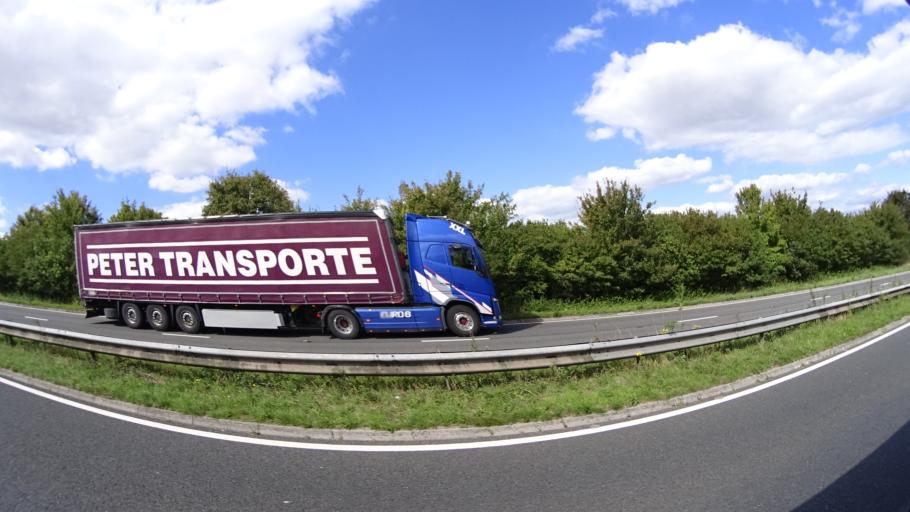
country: GB
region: England
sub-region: Wiltshire
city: Stockton
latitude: 51.1335
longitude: -2.0071
